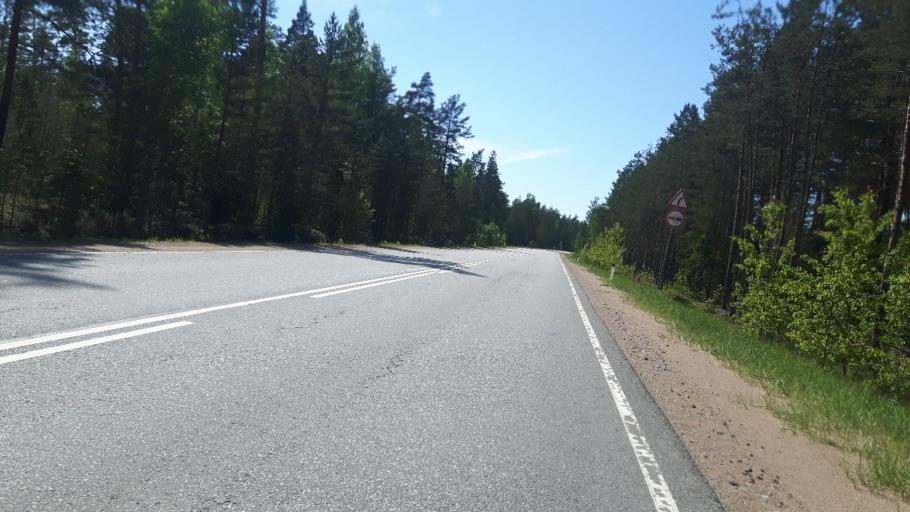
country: RU
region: Leningrad
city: Sista-Palkino
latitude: 59.7678
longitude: 28.8059
